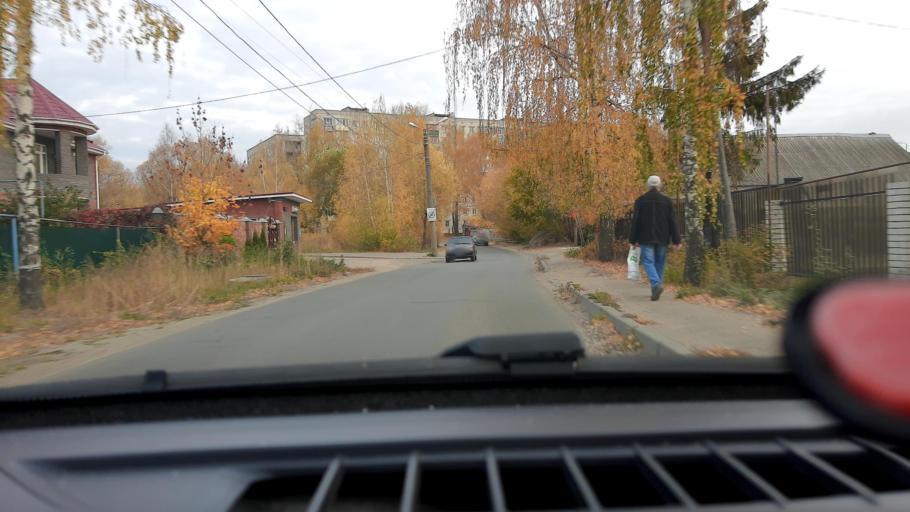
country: RU
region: Nizjnij Novgorod
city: Gorbatovka
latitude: 56.3386
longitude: 43.8304
